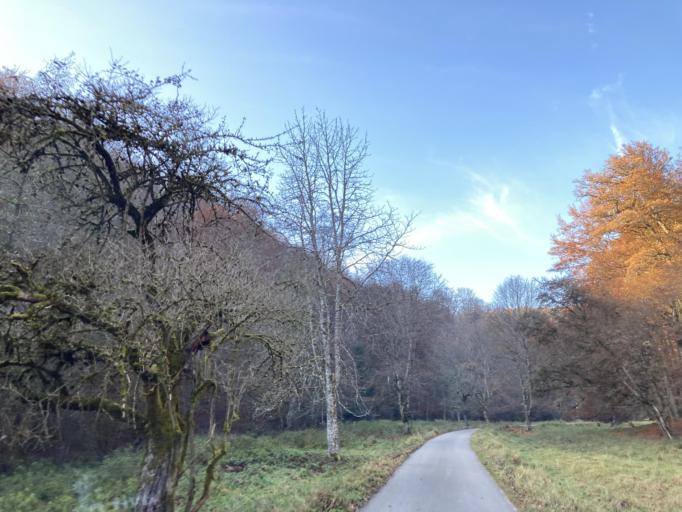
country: DE
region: Baden-Wuerttemberg
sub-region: Tuebingen Region
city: Tuebingen
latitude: 48.5635
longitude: 9.0352
